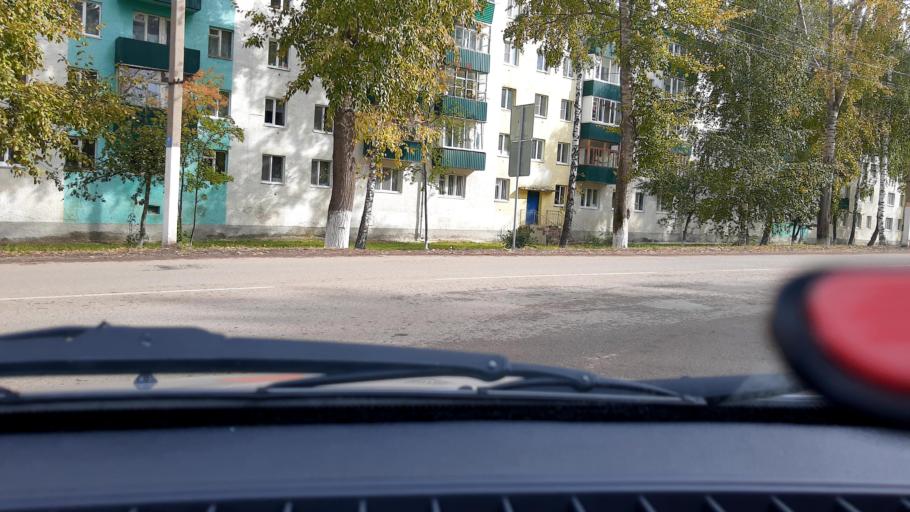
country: RU
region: Bashkortostan
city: Belebey
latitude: 54.1044
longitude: 54.0963
